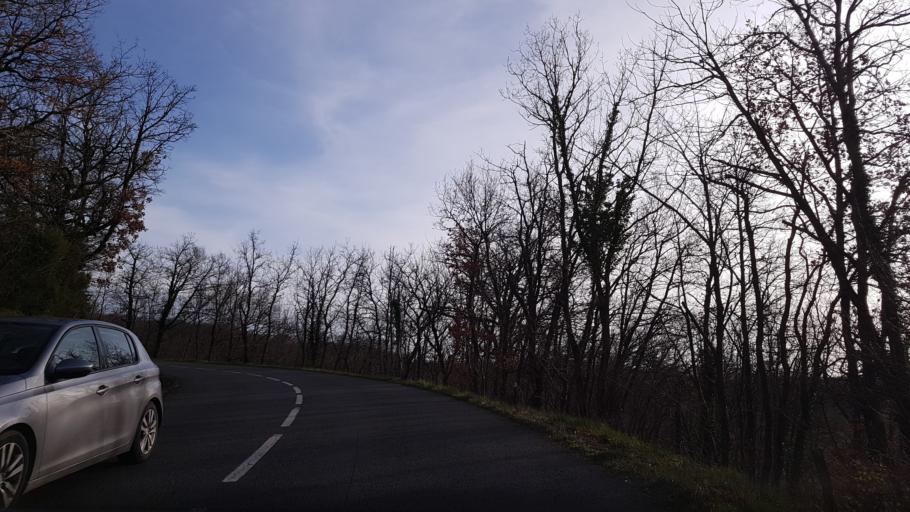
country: FR
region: Languedoc-Roussillon
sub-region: Departement de l'Aude
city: Villeneuve-la-Comptal
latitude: 43.2386
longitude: 1.9174
